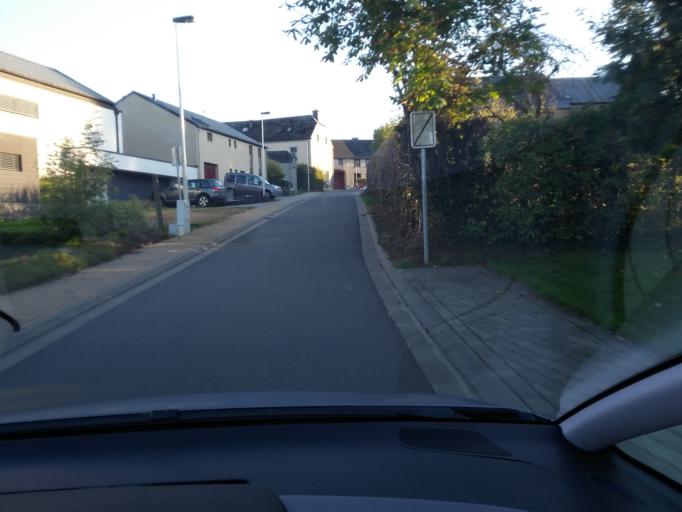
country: BE
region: Wallonia
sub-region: Province du Luxembourg
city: Arlon
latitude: 49.7011
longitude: 5.8301
